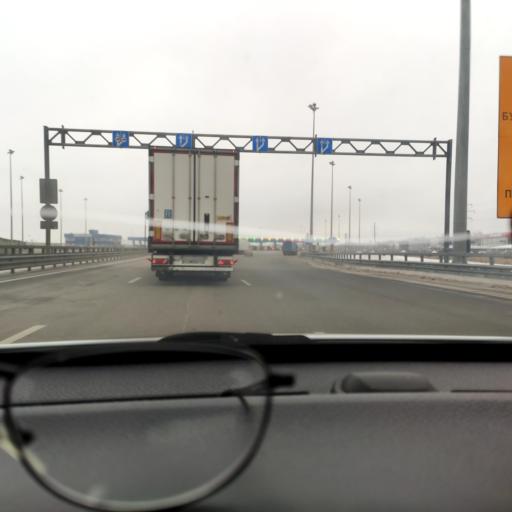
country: RU
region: Voronezj
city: Somovo
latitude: 51.6663
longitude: 39.3009
